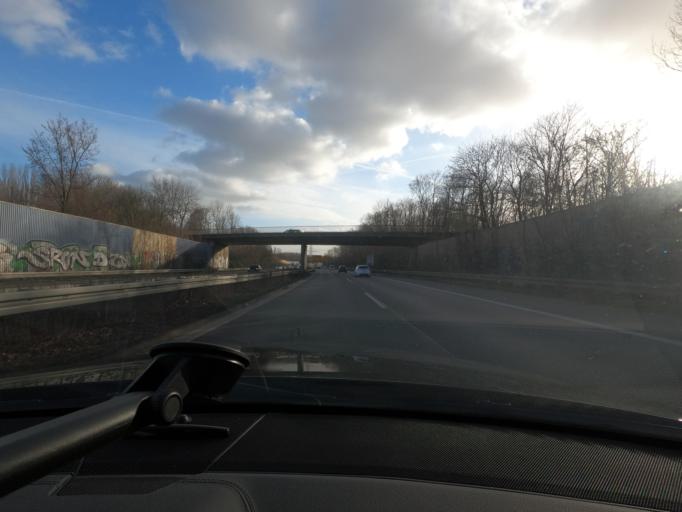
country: DE
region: North Rhine-Westphalia
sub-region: Regierungsbezirk Arnsberg
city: Dortmund
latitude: 51.5423
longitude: 7.5146
